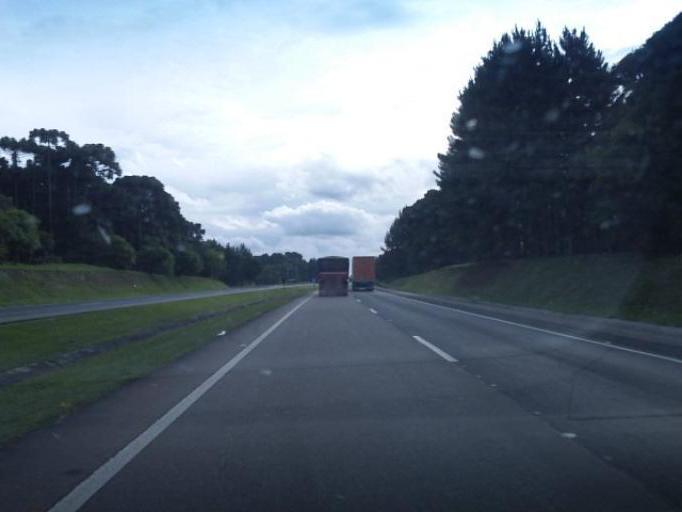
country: BR
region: Parana
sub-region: Piraquara
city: Piraquara
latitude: -25.4088
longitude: -49.0626
